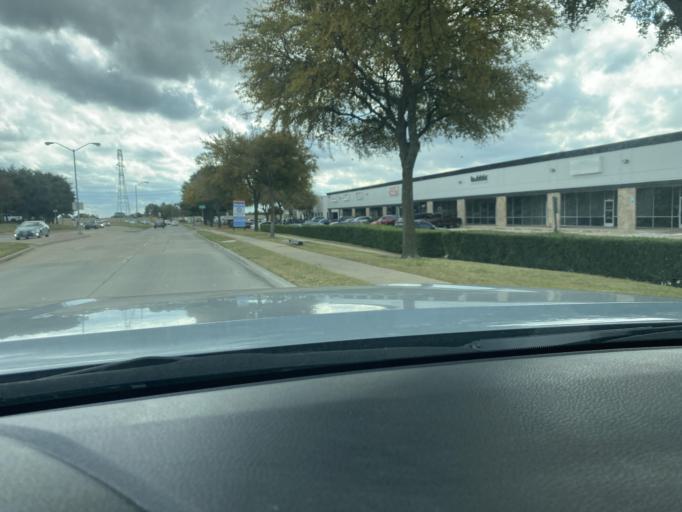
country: US
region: Texas
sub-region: Dallas County
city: Addison
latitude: 33.0141
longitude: -96.7868
